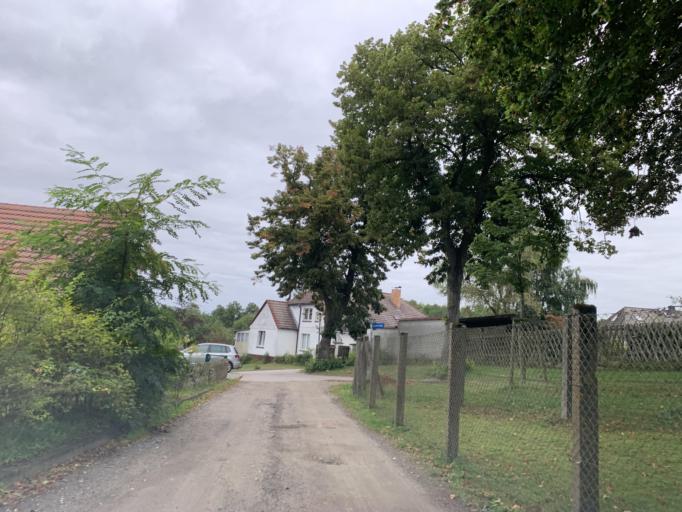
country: DE
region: Mecklenburg-Vorpommern
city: Loitz
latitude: 53.3340
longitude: 13.4414
